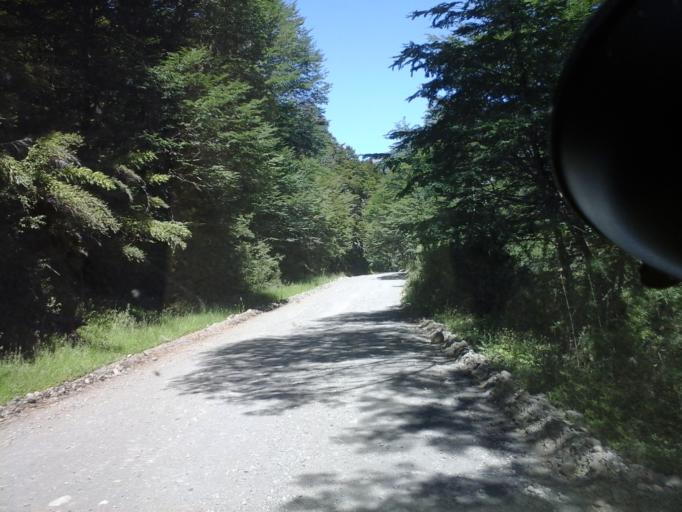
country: AR
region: Neuquen
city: Villa La Angostura
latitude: -41.2168
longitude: -71.7984
